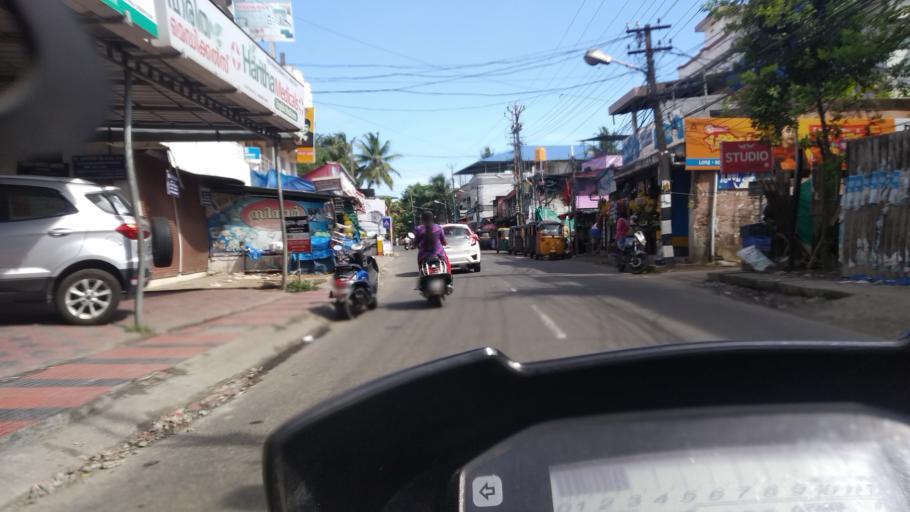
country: IN
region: Kerala
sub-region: Ernakulam
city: Elur
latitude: 10.0219
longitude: 76.2741
